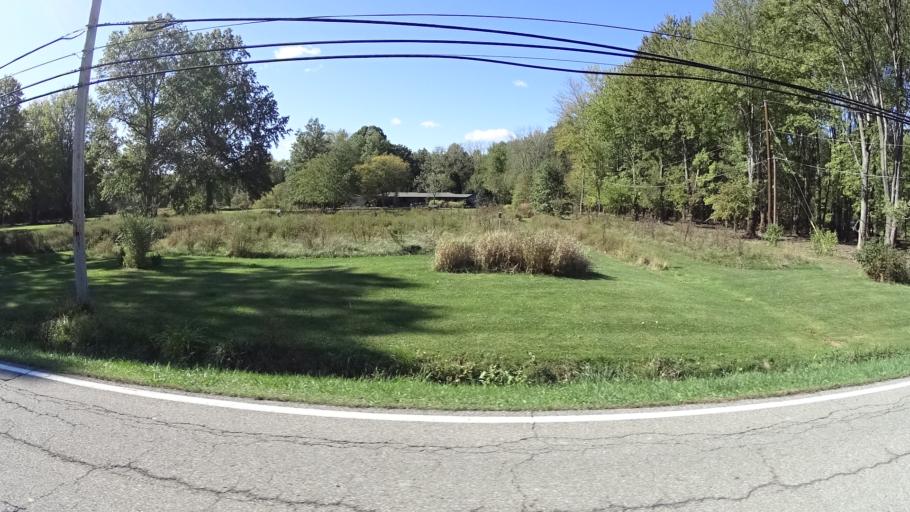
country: US
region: Ohio
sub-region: Lorain County
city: Elyria
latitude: 41.3290
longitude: -82.0904
